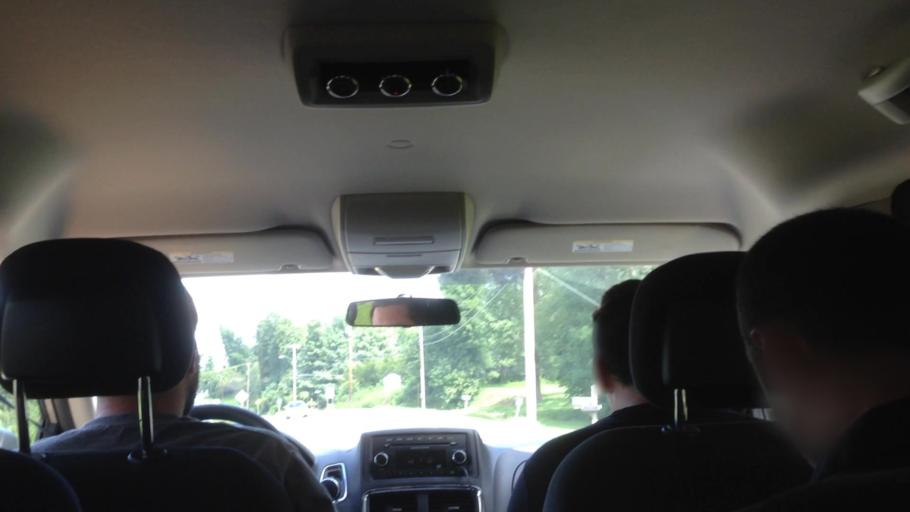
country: US
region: New York
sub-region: Dutchess County
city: Red Hook
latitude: 42.0201
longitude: -73.8504
